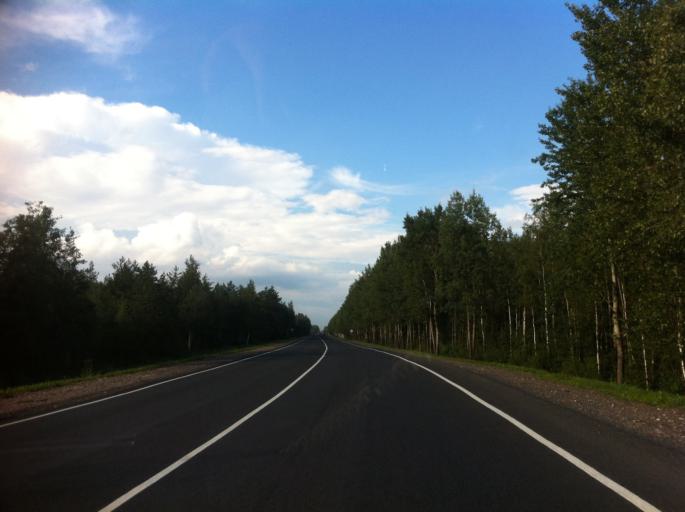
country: RU
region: Leningrad
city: Luga
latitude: 58.4413
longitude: 29.7522
